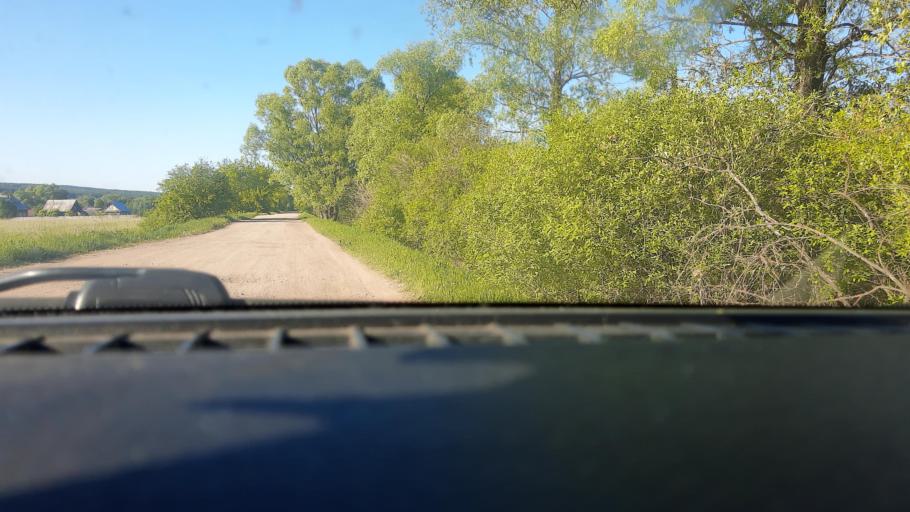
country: RU
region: Bashkortostan
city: Ulukulevo
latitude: 54.5575
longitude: 56.3262
